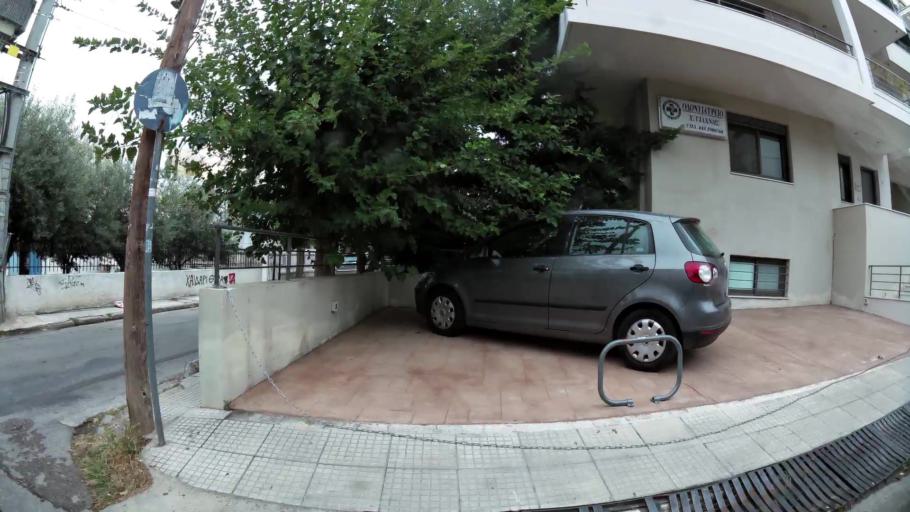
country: GR
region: Attica
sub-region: Nomarchia Athinas
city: Chaidari
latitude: 38.0025
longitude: 23.6652
